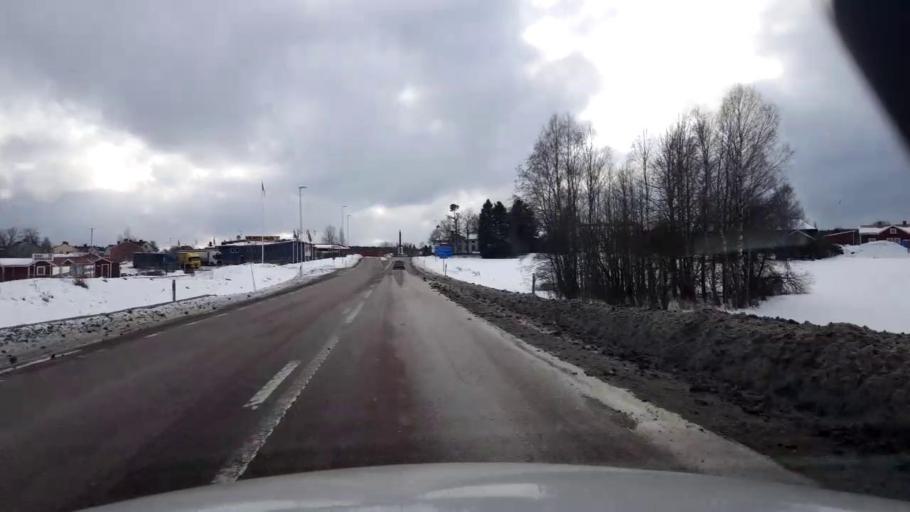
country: SE
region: Gaevleborg
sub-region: Nordanstigs Kommun
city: Bergsjoe
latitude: 61.9313
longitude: 17.2162
